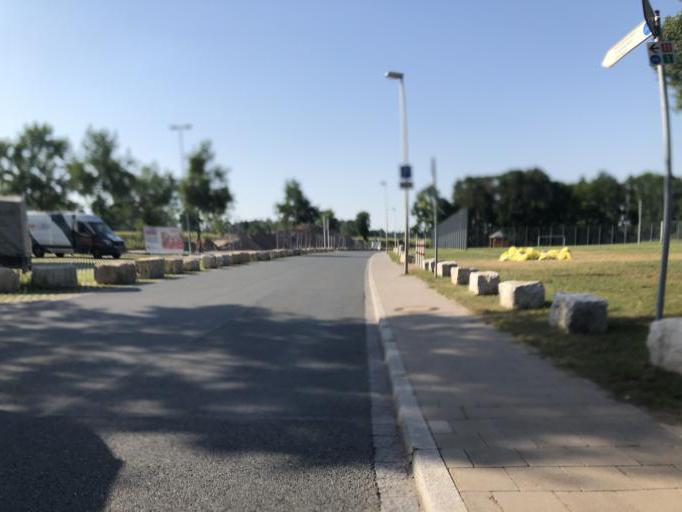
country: DE
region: Bavaria
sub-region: Regierungsbezirk Mittelfranken
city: Erlangen
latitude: 49.5659
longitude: 10.9718
